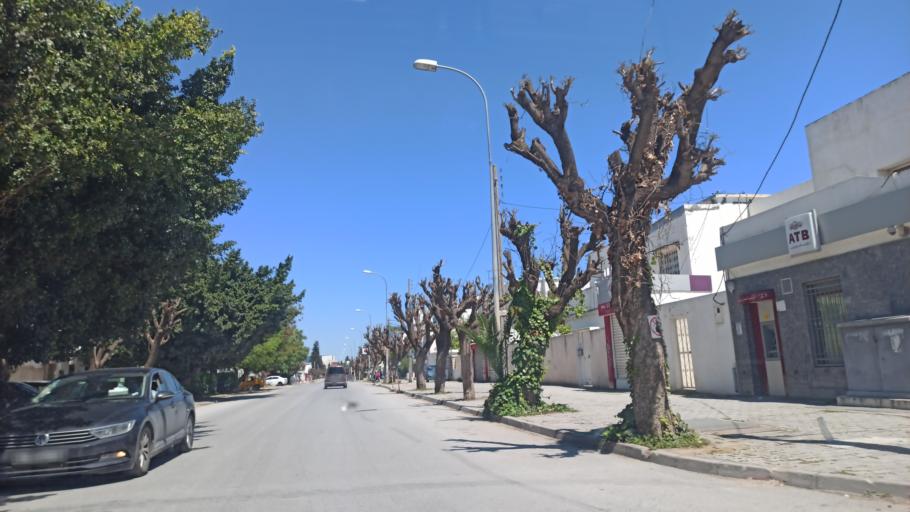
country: TN
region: Tunis
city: Tunis
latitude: 36.8267
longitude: 10.1835
